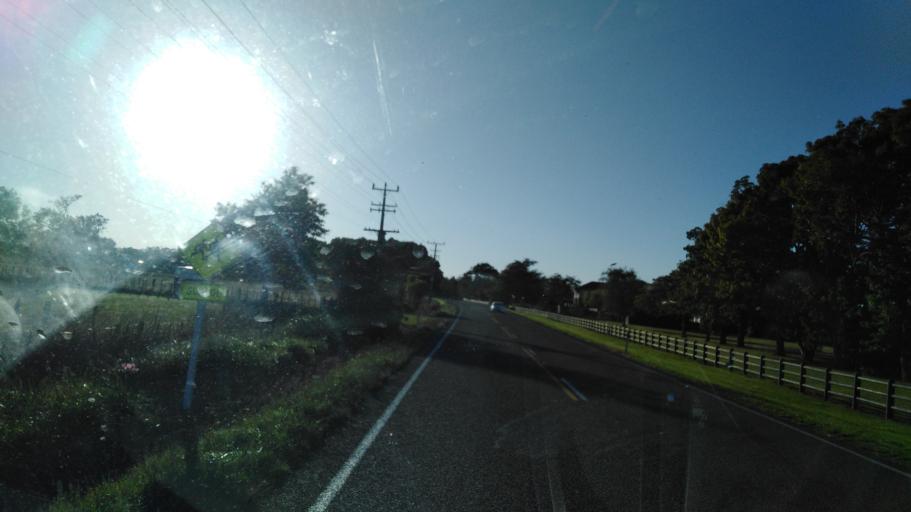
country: NZ
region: Manawatu-Wanganui
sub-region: Rangitikei District
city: Bulls
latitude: -40.0662
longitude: 175.3961
